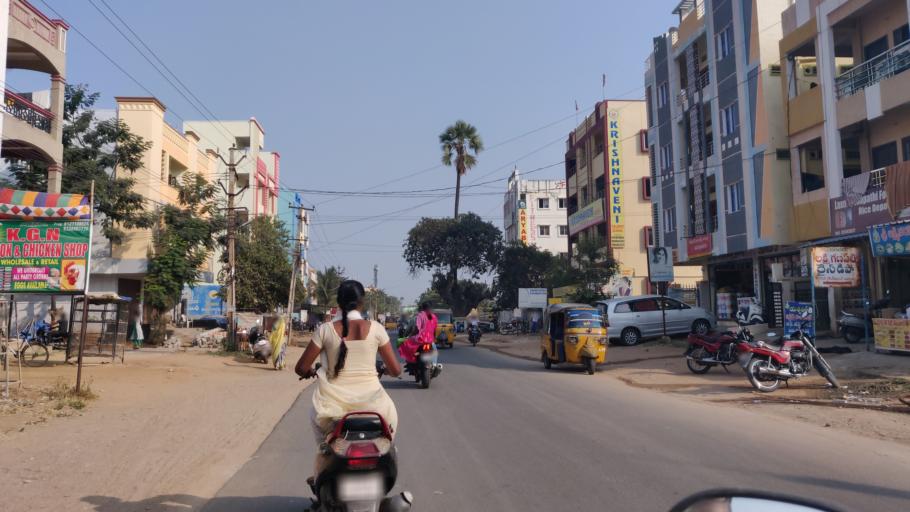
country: IN
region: Telangana
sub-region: Rangareddi
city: Uppal Kalan
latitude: 17.3919
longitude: 78.5983
